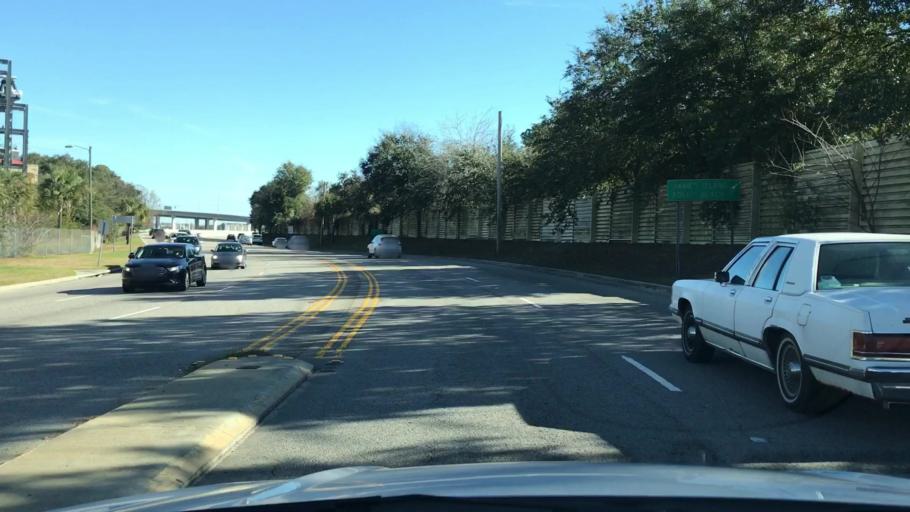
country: US
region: South Carolina
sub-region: Charleston County
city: Charleston
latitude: 32.7754
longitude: -79.9642
